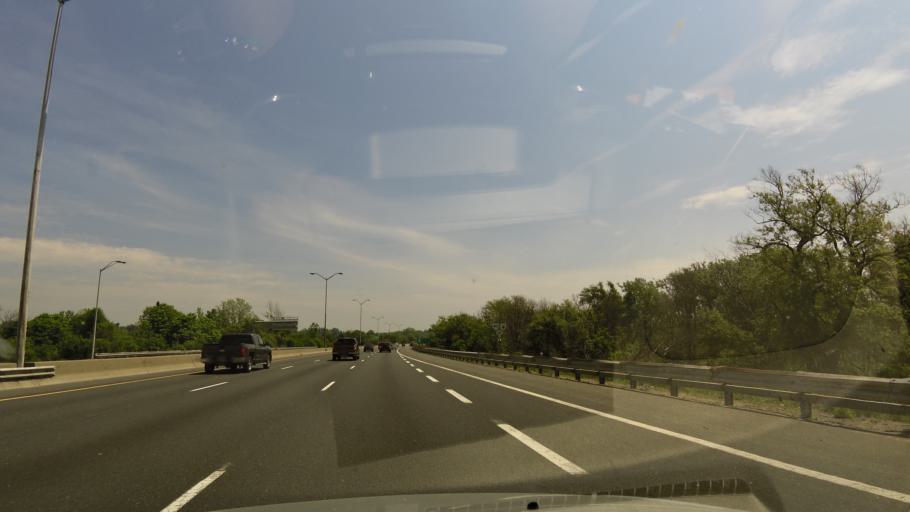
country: CA
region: Ontario
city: Oshawa
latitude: 43.8871
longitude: -78.8258
